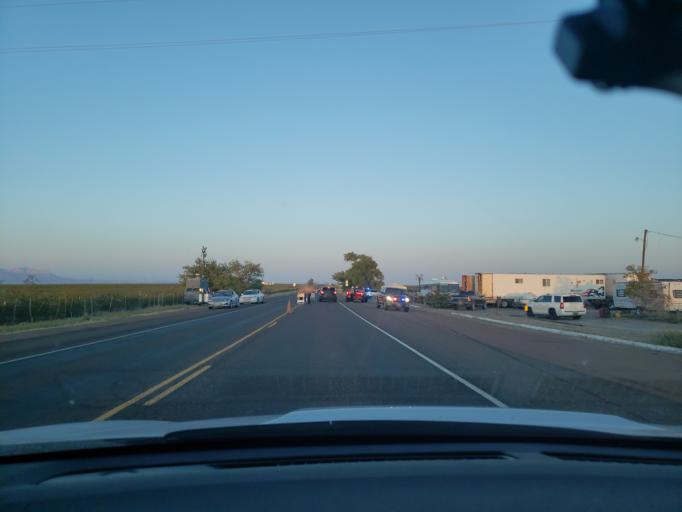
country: US
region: Texas
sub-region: Hudspeth County
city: Sierra Blanca
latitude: 31.7614
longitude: -105.3677
